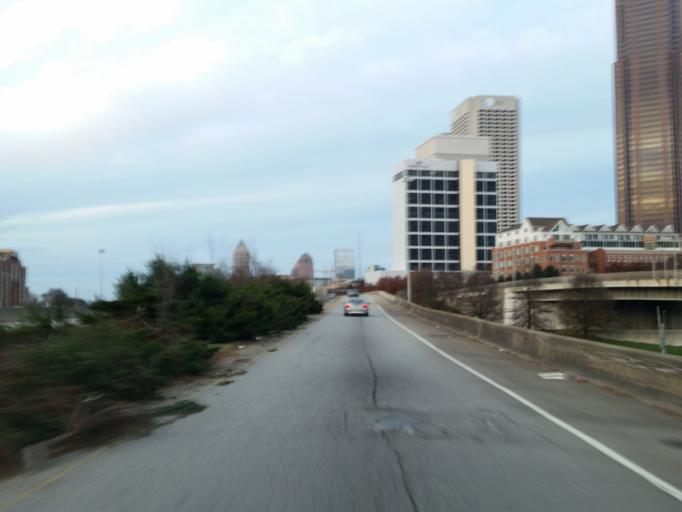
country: US
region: Georgia
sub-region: Fulton County
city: Atlanta
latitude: 33.7665
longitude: -84.3901
